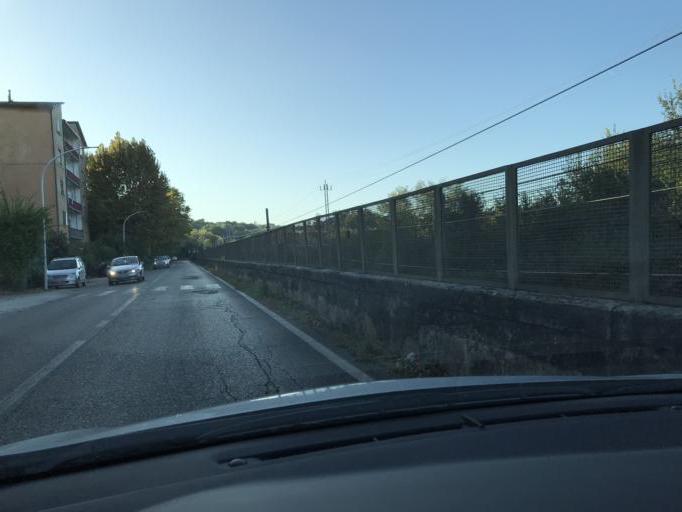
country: IT
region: Latium
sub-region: Provincia di Viterbo
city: Orte Scalo
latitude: 42.4458
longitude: 12.3963
